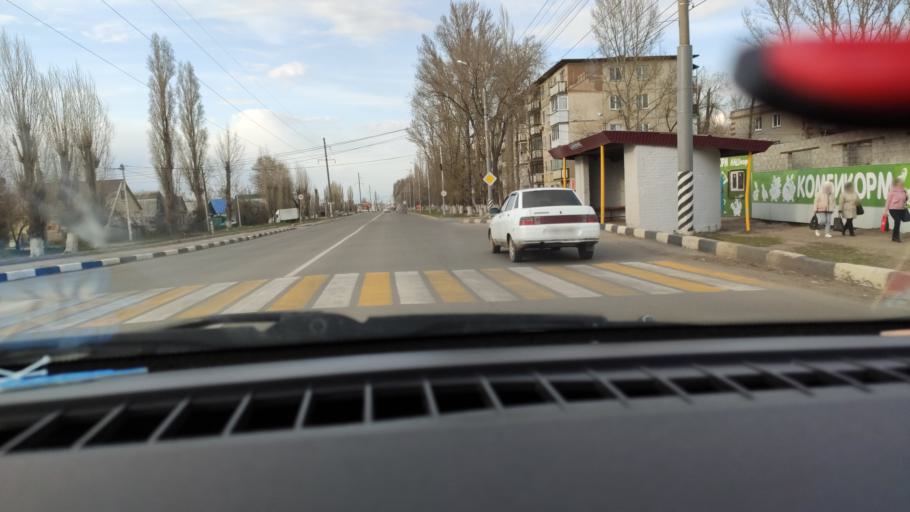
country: RU
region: Saratov
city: Privolzhskiy
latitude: 51.4068
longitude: 46.0397
